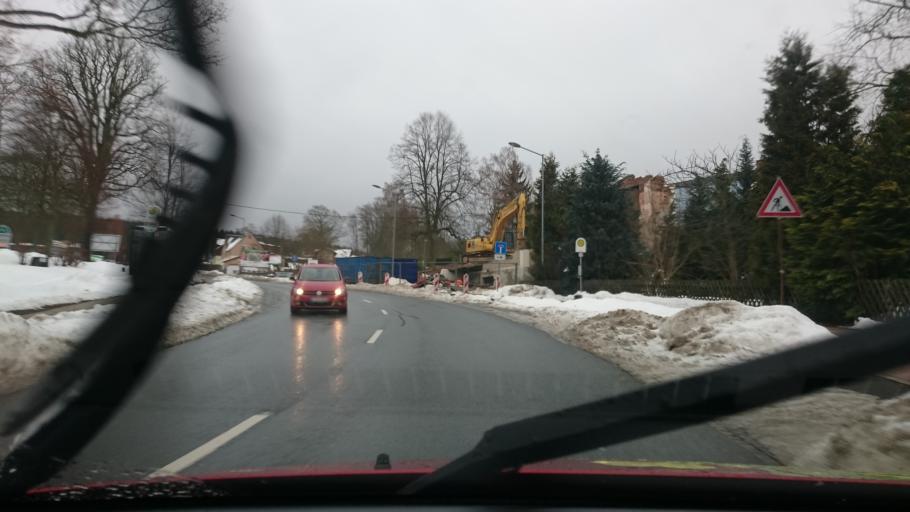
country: DE
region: Saxony
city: Erlbach
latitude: 50.3225
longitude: 12.3471
